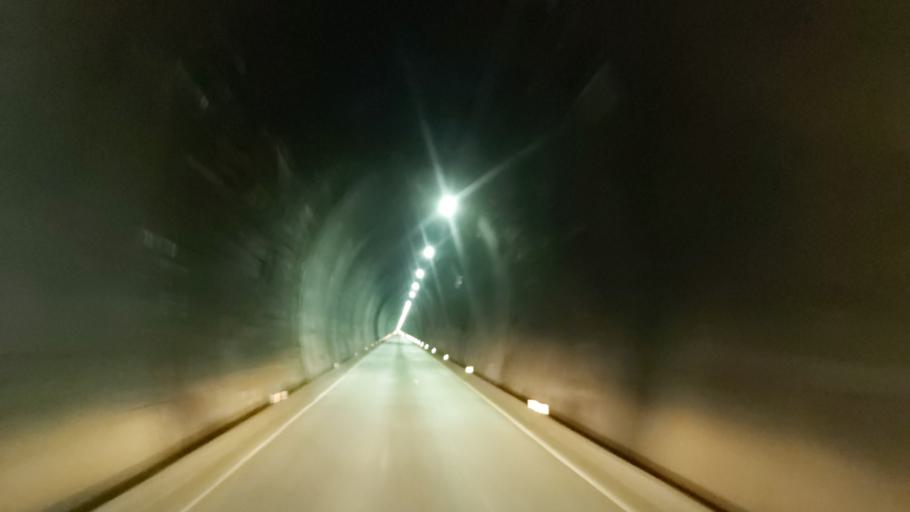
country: CL
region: Araucania
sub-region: Provincia de Cautin
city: Vilcun
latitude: -38.5441
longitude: -71.5046
